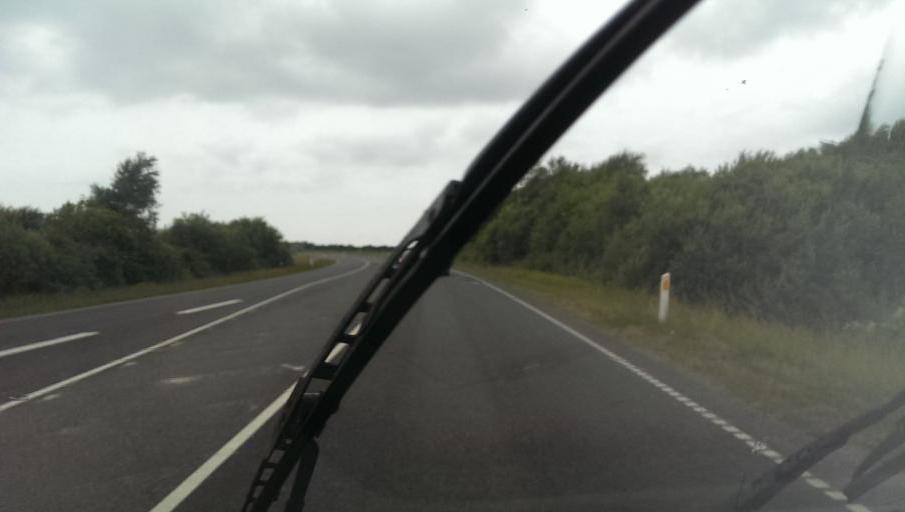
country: DK
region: South Denmark
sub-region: Esbjerg Kommune
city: Tjaereborg
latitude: 55.5048
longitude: 8.5392
